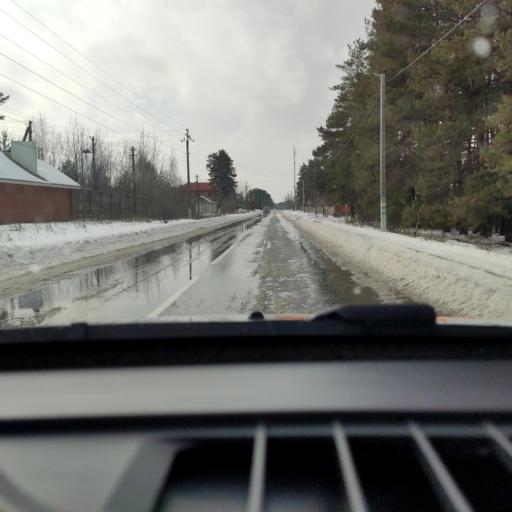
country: RU
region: Voronezj
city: Podgornoye
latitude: 51.7823
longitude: 39.1381
